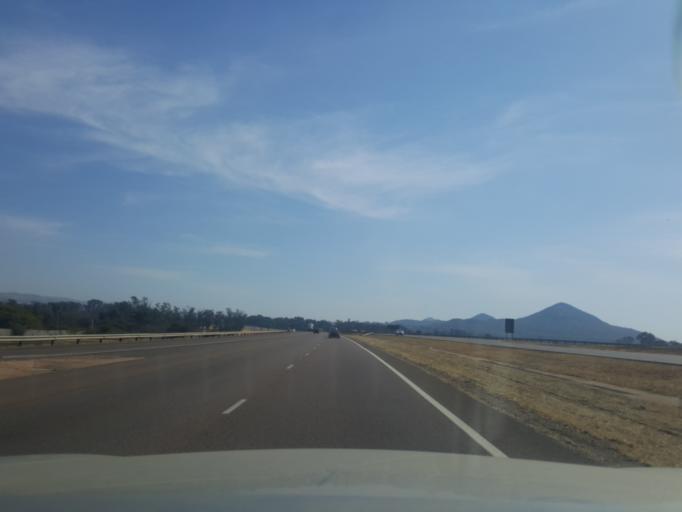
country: ZA
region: Gauteng
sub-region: City of Tshwane Metropolitan Municipality
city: Pretoria
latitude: -25.6381
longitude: 28.2022
